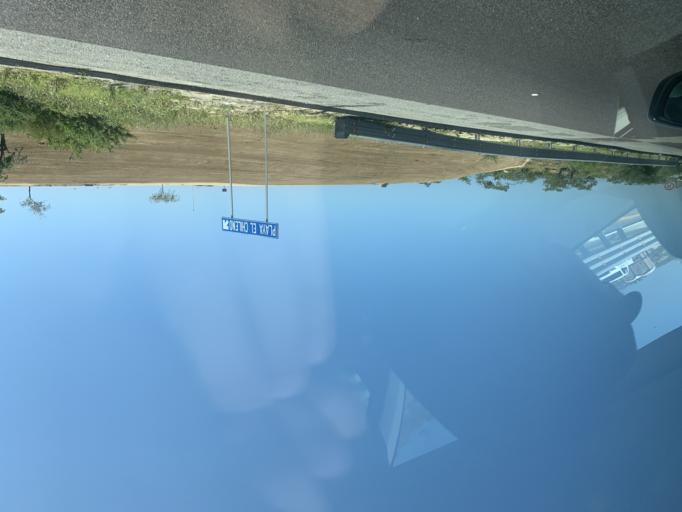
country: MX
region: Baja California Sur
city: Cabo San Lucas
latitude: 22.9496
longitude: -109.8138
